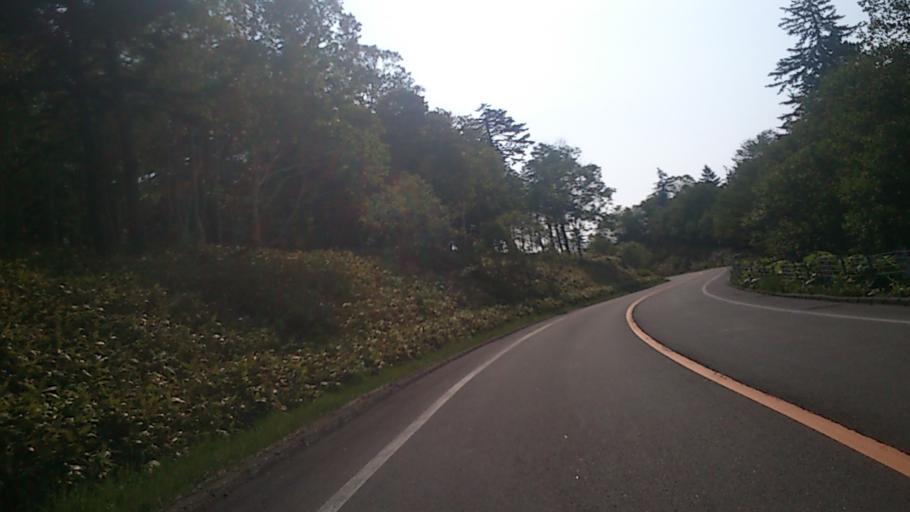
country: JP
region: Hokkaido
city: Bihoro
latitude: 43.4432
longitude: 144.1923
